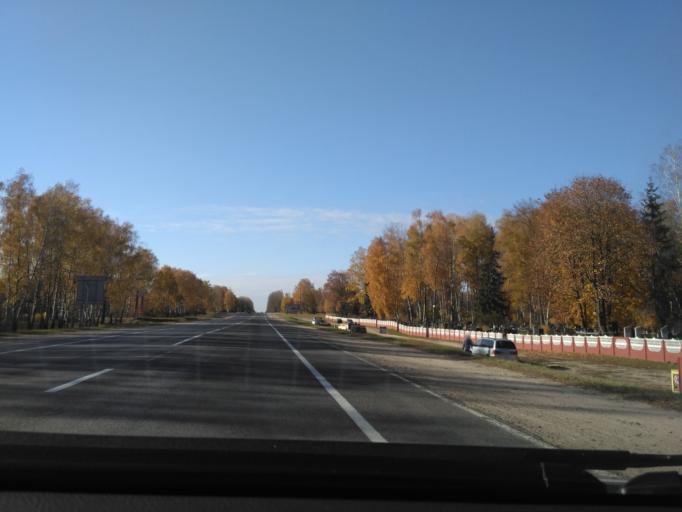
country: BY
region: Minsk
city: Horad Barysaw
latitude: 54.2544
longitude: 28.5683
